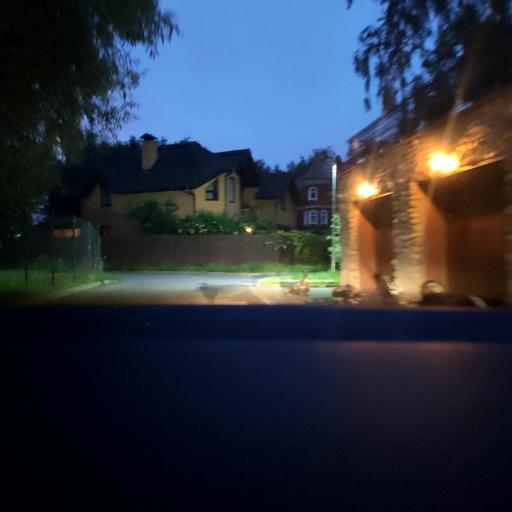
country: RU
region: Moscow
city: Severnyy
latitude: 55.9351
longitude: 37.5320
